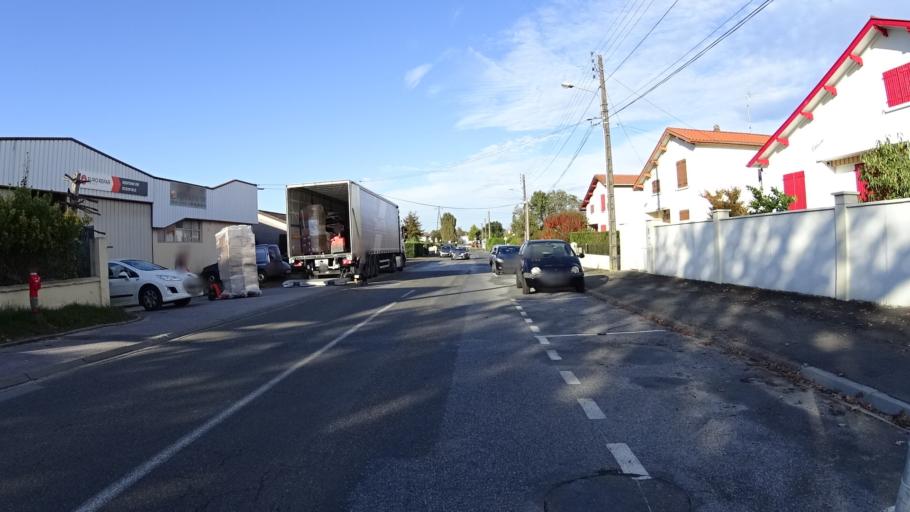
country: FR
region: Aquitaine
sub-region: Departement des Landes
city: Saint-Paul-les-Dax
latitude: 43.7331
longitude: -1.0554
